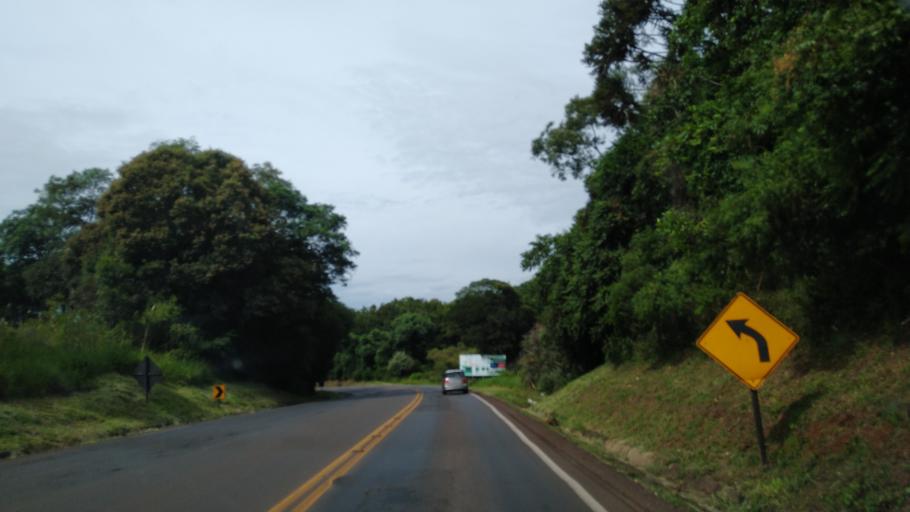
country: BR
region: Parana
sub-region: Francisco Beltrao
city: Francisco Beltrao
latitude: -26.1625
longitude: -52.9508
